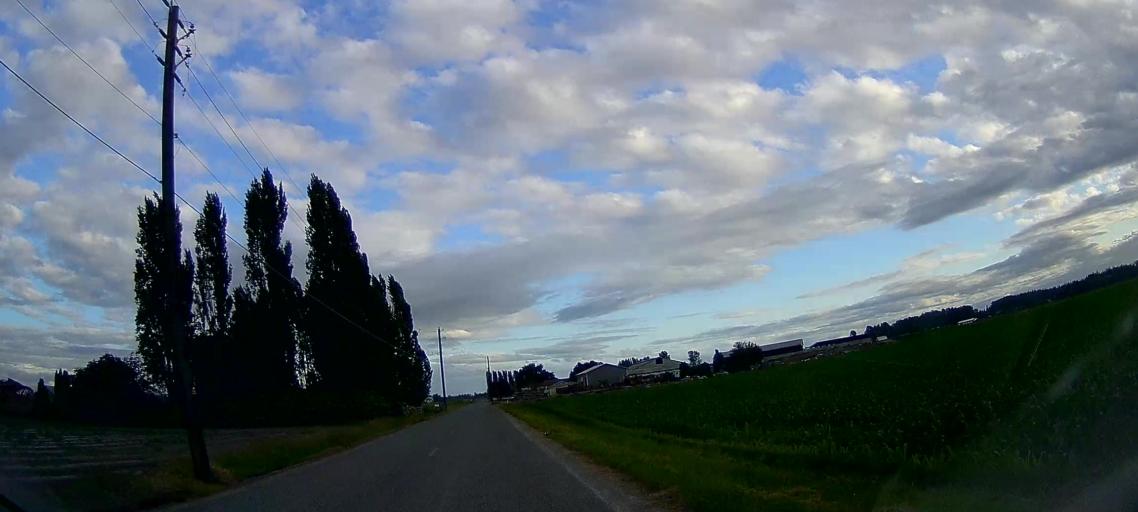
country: US
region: Washington
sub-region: Skagit County
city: Mount Vernon
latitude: 48.3774
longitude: -122.4006
